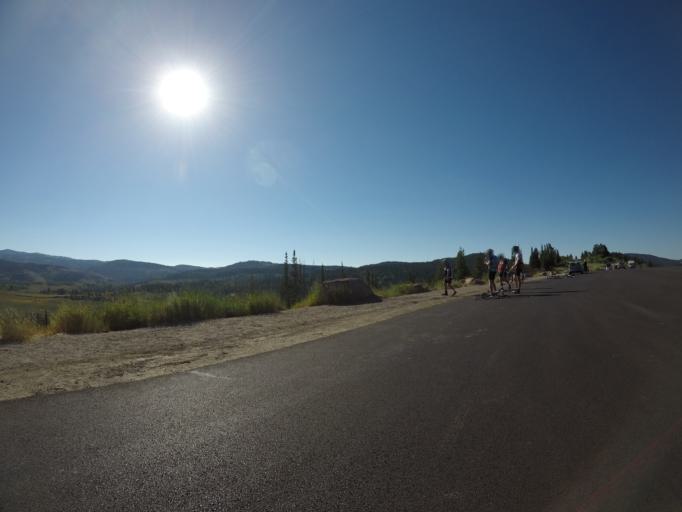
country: US
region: Wyoming
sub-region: Lincoln County
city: Afton
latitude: 42.5068
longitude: -110.9085
